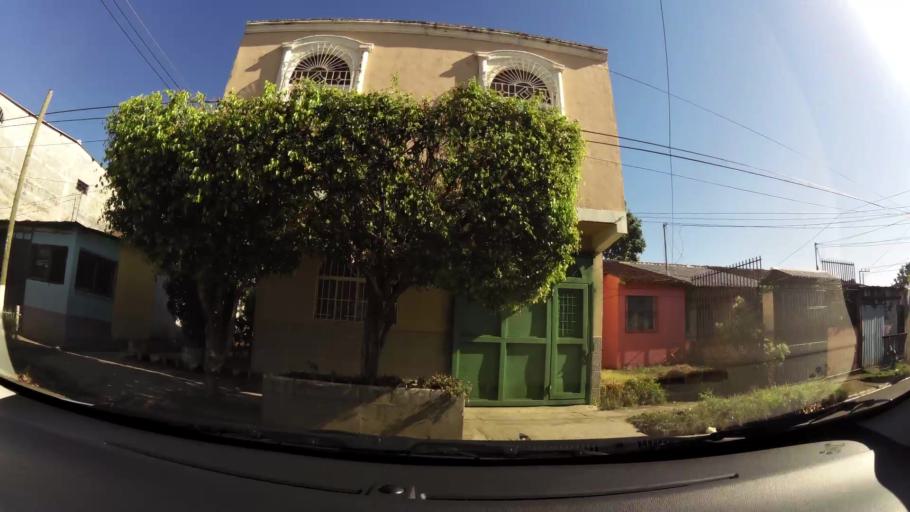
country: SV
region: Sonsonate
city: Sonzacate
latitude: 13.7409
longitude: -89.7135
